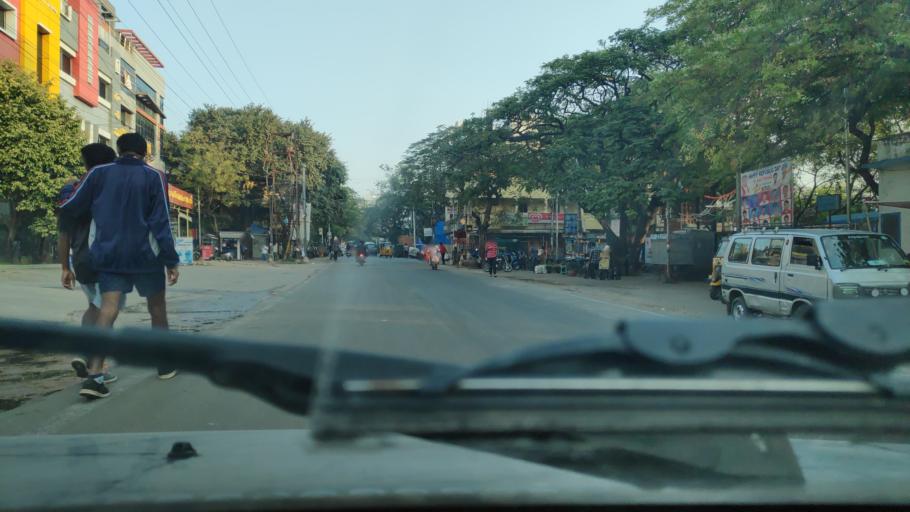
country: IN
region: Telangana
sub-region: Rangareddi
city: Gaddi Annaram
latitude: 17.3637
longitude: 78.5217
